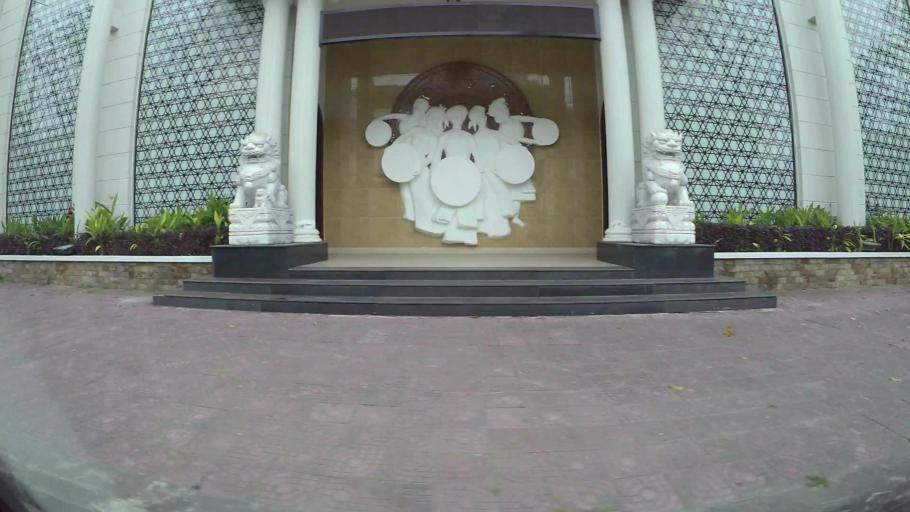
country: VN
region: Da Nang
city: Da Nang
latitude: 16.0517
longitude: 108.2119
